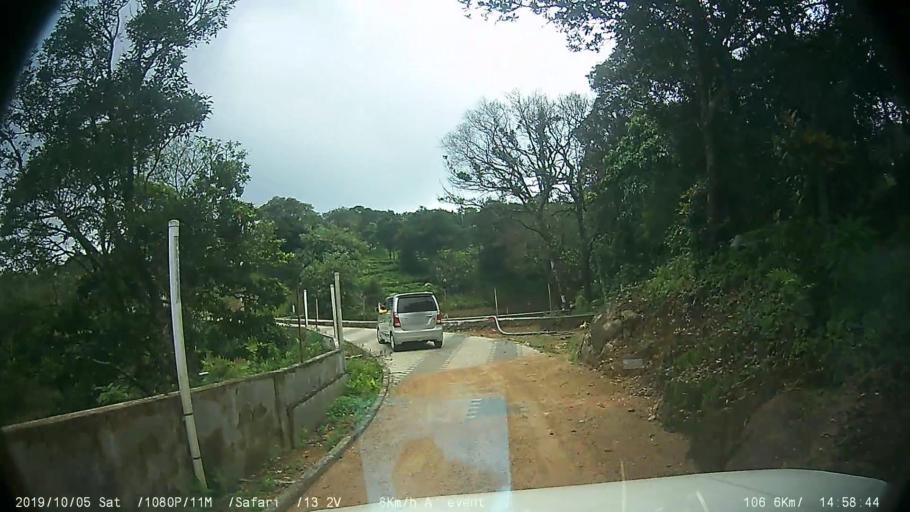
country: IN
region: Kerala
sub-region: Kottayam
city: Erattupetta
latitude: 9.6202
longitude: 76.9345
